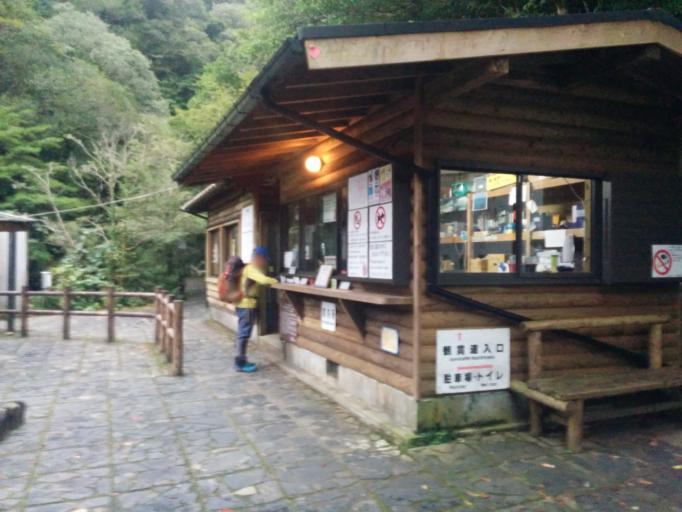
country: JP
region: Kagoshima
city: Nishinoomote
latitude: 30.3799
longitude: 130.5741
